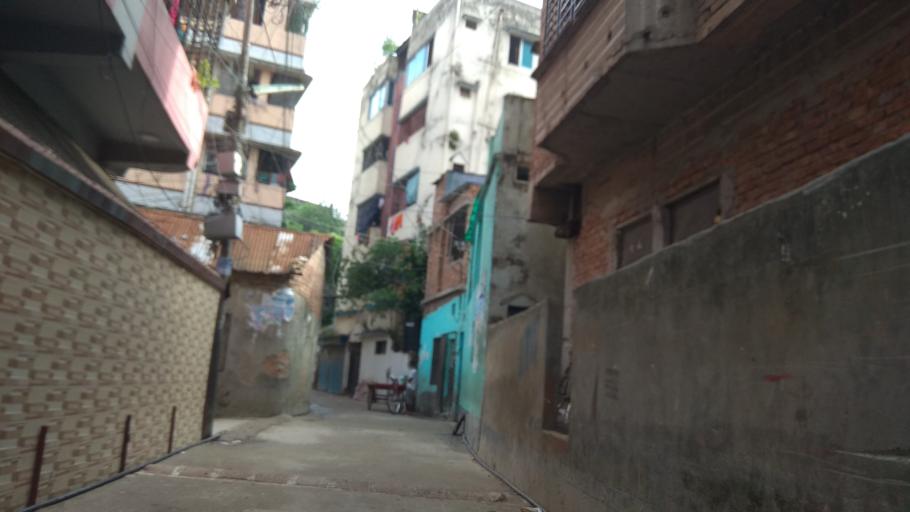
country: BD
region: Dhaka
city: Azimpur
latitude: 23.7928
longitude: 90.3833
